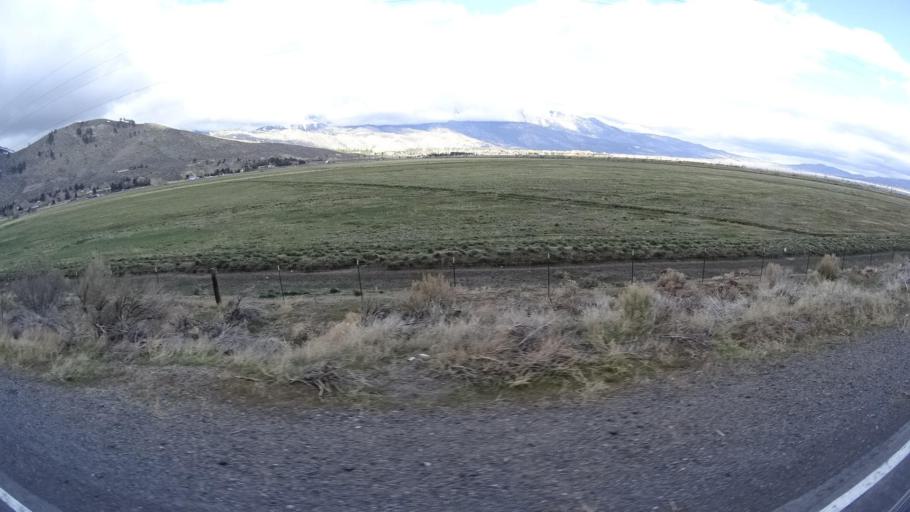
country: US
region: Nevada
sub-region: Carson City
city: Carson City
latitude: 39.2219
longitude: -119.7997
